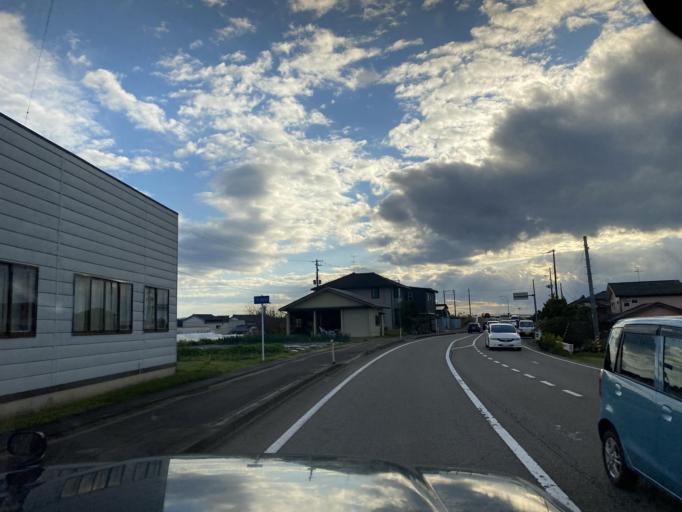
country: JP
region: Niigata
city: Kamo
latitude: 37.6737
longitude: 139.0129
